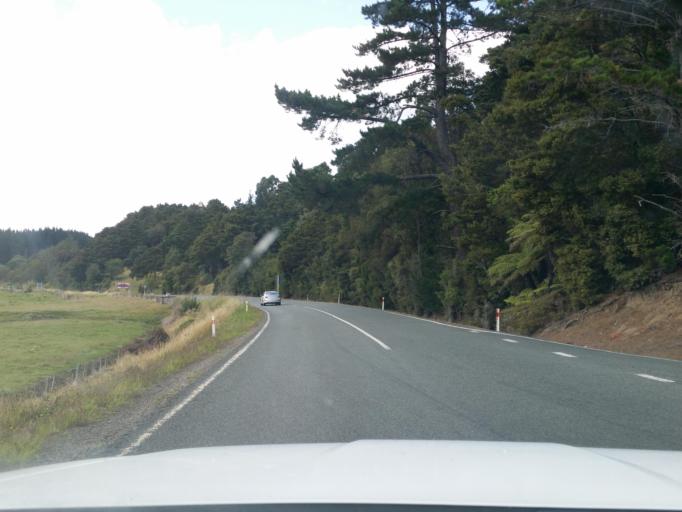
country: NZ
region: Northland
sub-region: Kaipara District
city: Dargaville
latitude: -35.8099
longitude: 173.7287
